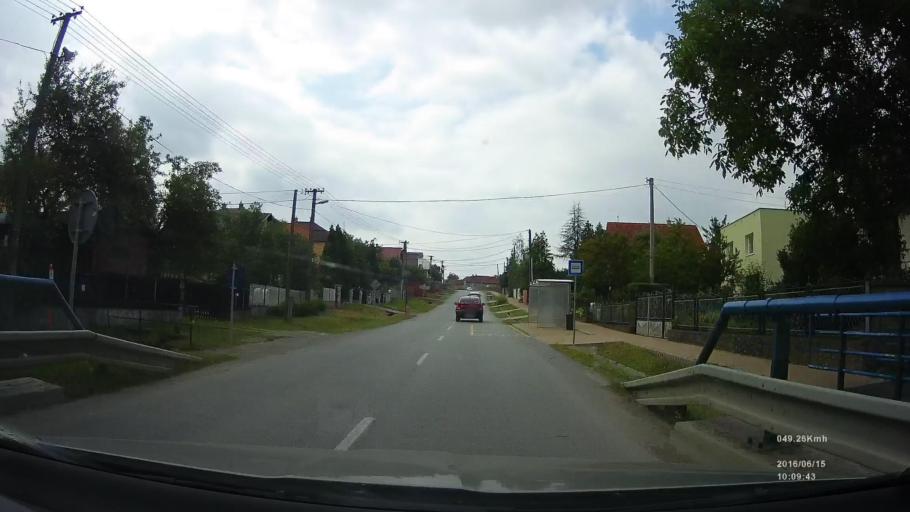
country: SK
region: Kosicky
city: Kosice
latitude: 48.7574
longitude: 21.3415
